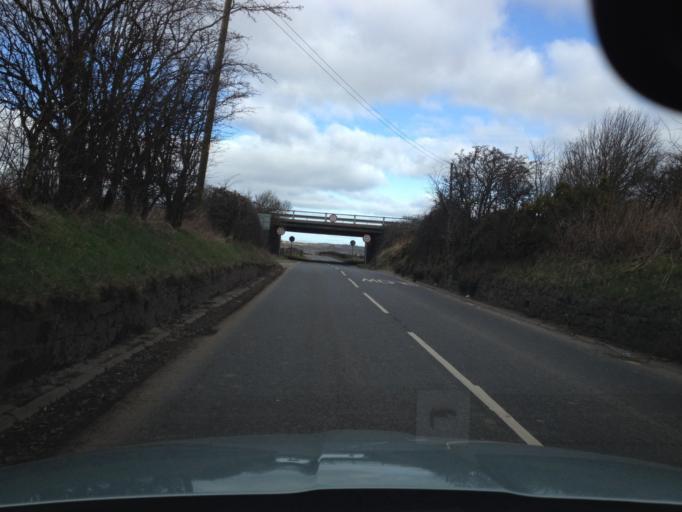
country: GB
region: Scotland
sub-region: West Lothian
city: Broxburn
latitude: 55.9216
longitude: -3.4647
